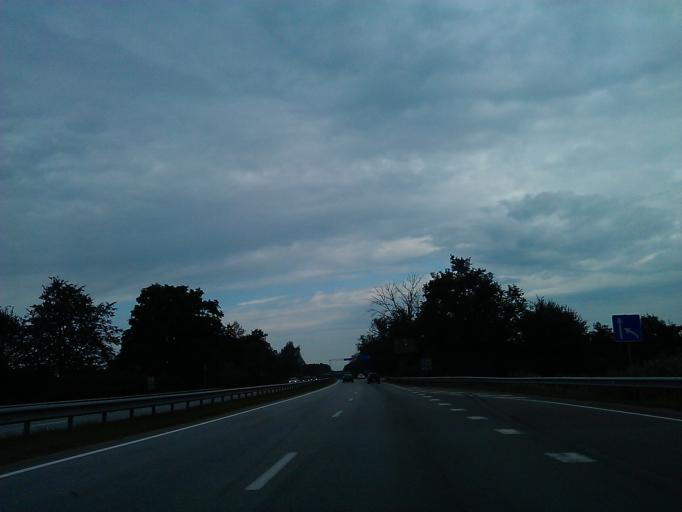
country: LV
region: Salaspils
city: Salaspils
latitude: 56.8562
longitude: 24.3209
